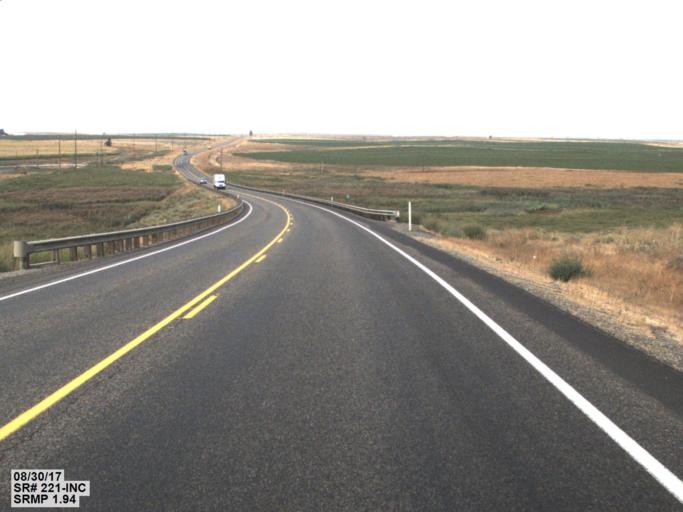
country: US
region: Oregon
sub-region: Morrow County
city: Irrigon
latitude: 45.9648
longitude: -119.6021
